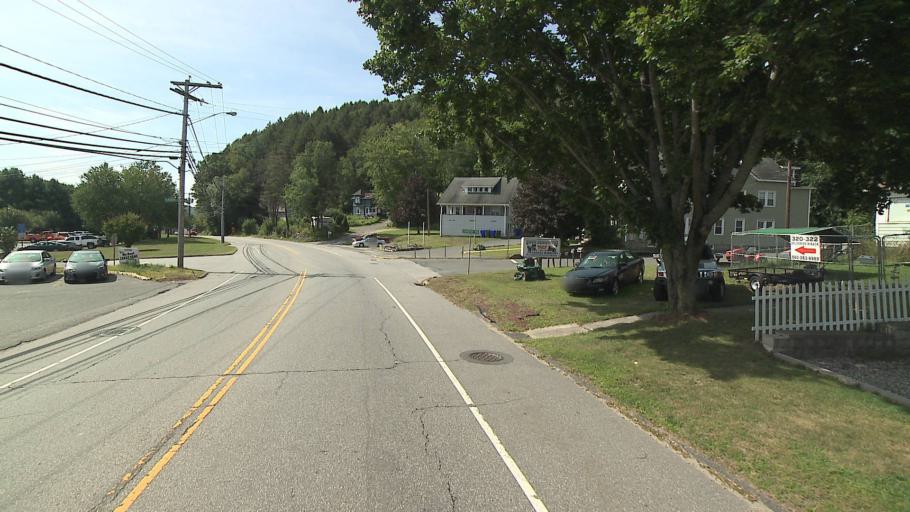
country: US
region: Connecticut
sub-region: Litchfield County
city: Thomaston
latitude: 41.6661
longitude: -73.0799
